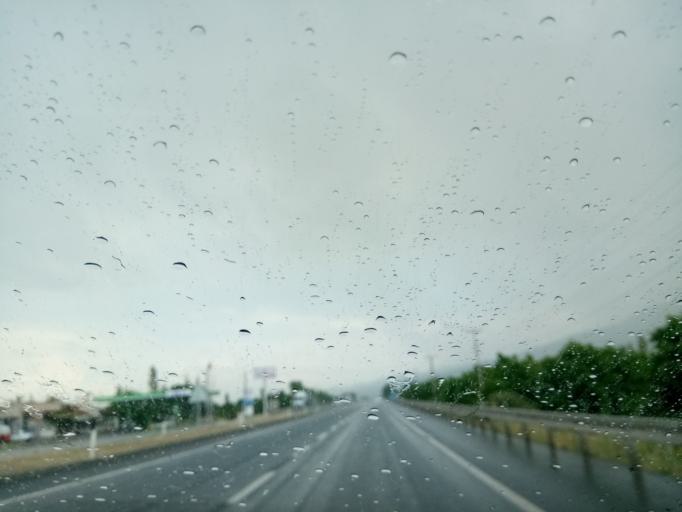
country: TR
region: Afyonkarahisar
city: Sultandagi
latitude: 38.5353
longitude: 31.2419
